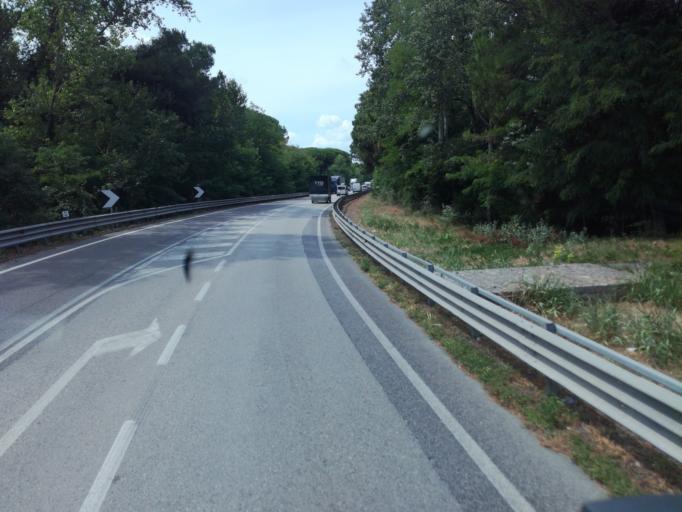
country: IT
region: Emilia-Romagna
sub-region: Provincia di Ferrara
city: Mesola
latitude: 44.9007
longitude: 12.2276
